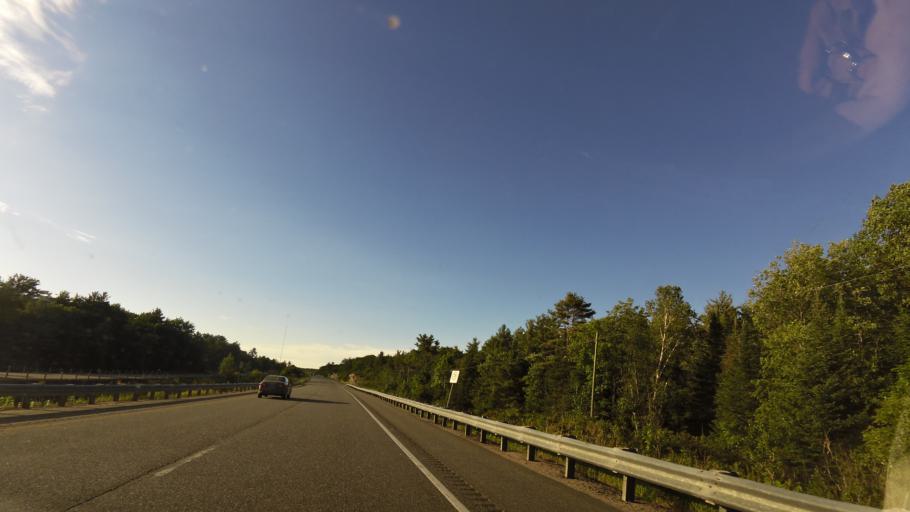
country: CA
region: Ontario
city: Midland
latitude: 44.9354
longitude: -79.7744
